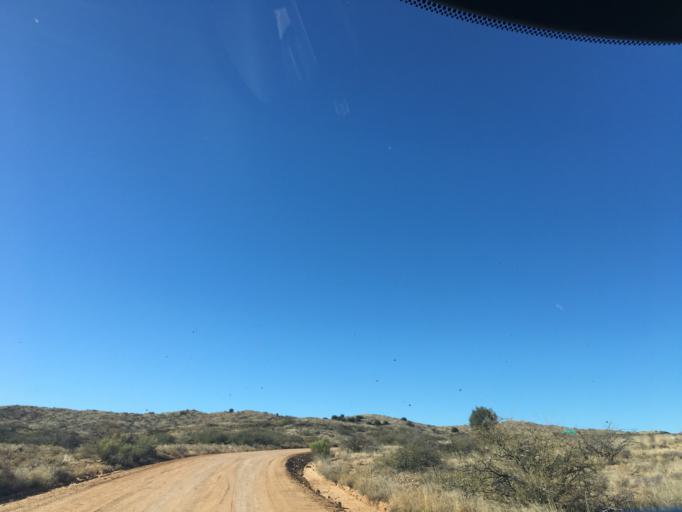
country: US
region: Arizona
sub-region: Yavapai County
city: Cordes Lakes
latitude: 34.2711
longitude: -112.1101
